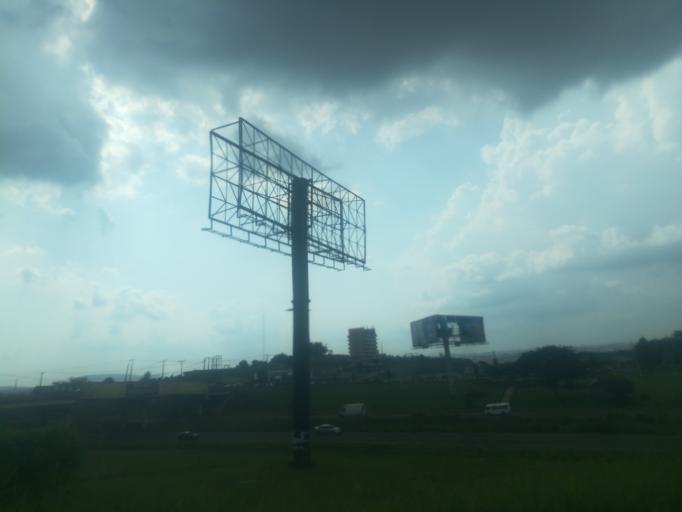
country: NG
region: Oyo
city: Ibadan
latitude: 7.3306
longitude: 3.8762
